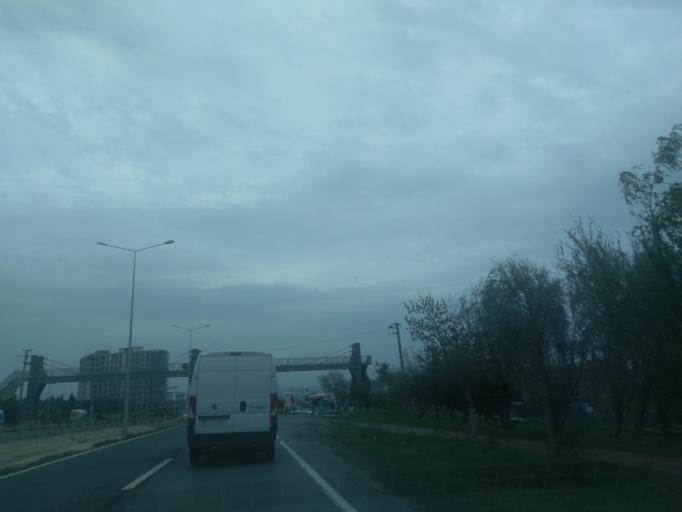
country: TR
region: Istanbul
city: Silivri
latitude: 41.0815
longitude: 28.2185
